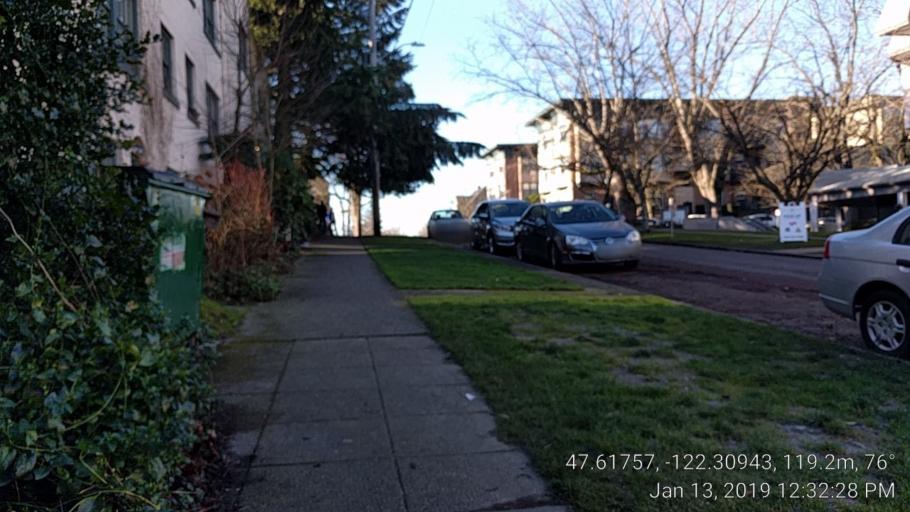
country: US
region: Washington
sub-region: King County
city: Seattle
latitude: 47.6176
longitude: -122.3094
